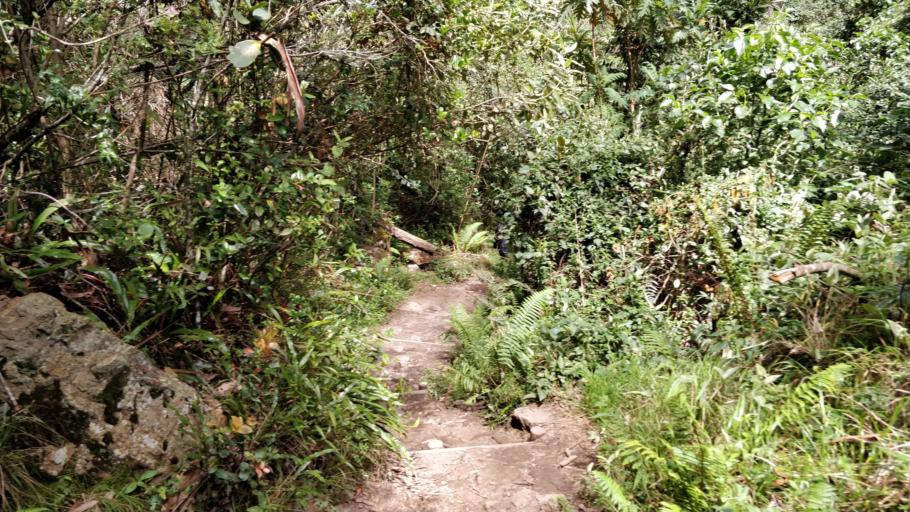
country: CO
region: Bogota D.C.
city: Barrio San Luis
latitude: 4.6449
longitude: -74.0434
